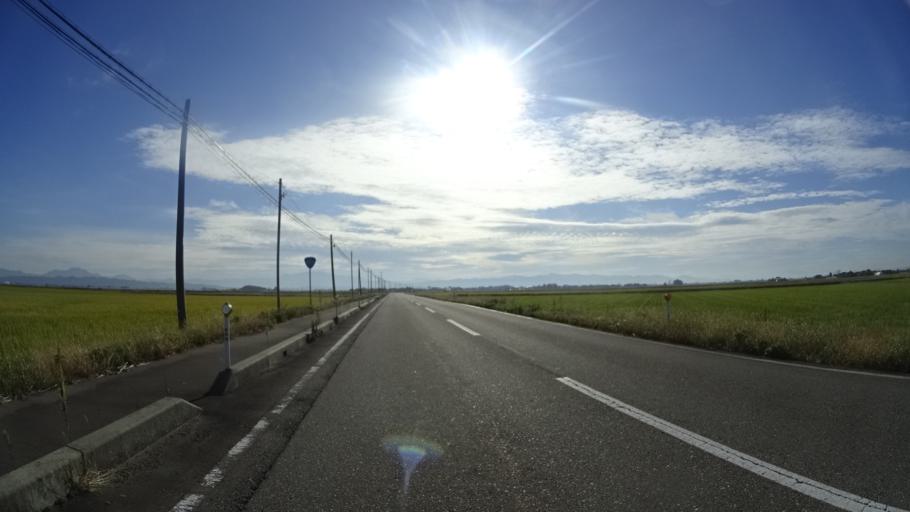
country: JP
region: Niigata
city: Mitsuke
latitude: 37.5686
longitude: 138.8432
